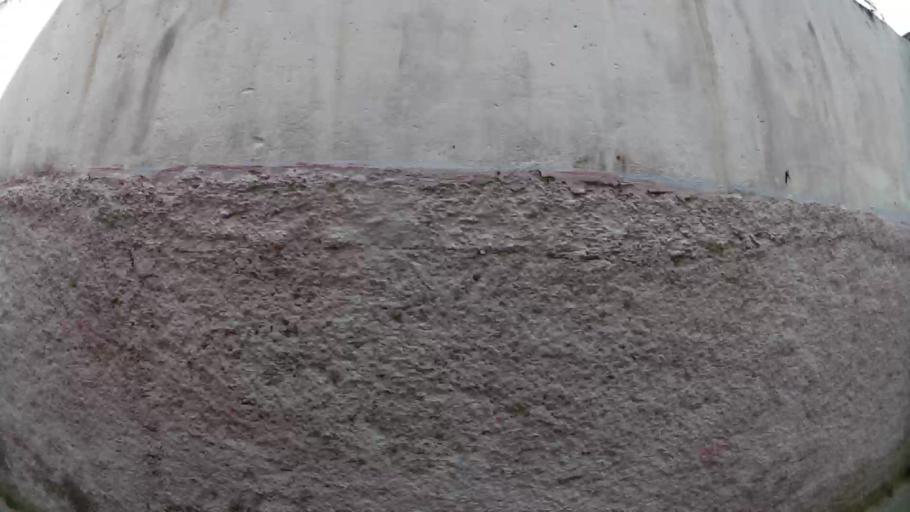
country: MA
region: Tanger-Tetouan
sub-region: Tanger-Assilah
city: Tangier
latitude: 35.7595
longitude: -5.7967
